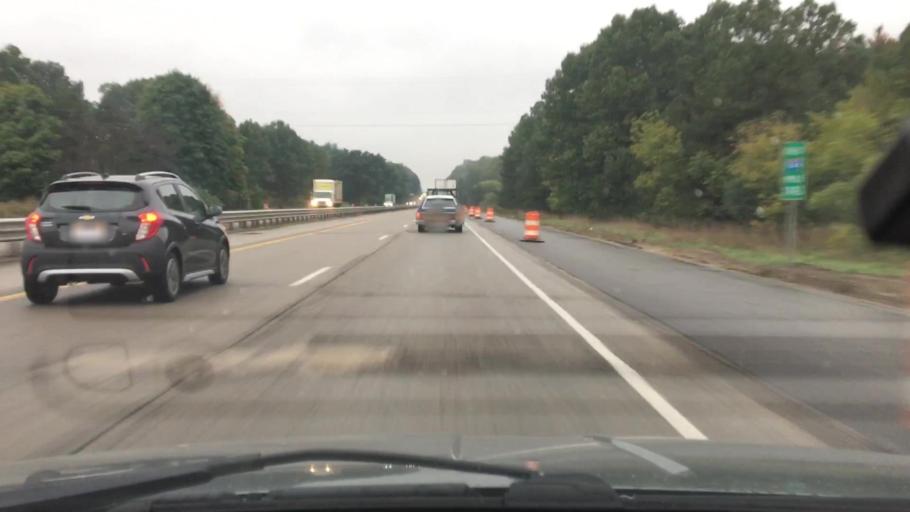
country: US
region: Michigan
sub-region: Jackson County
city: Michigan Center
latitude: 42.2775
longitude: -84.3376
